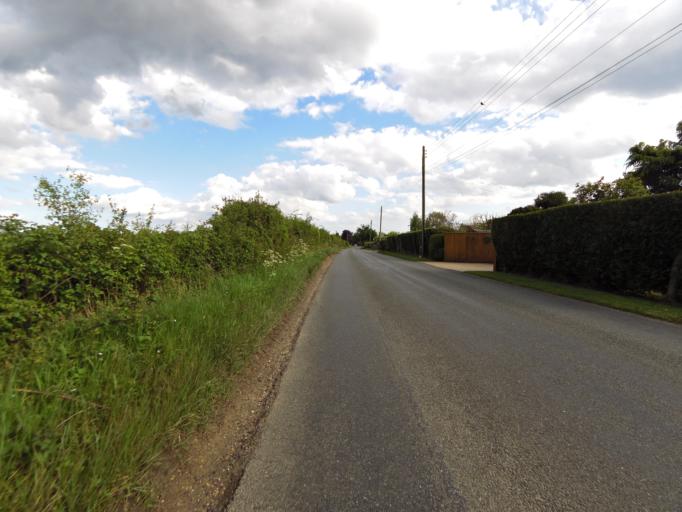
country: GB
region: England
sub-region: Suffolk
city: Elmswell
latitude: 52.2096
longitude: 0.9172
